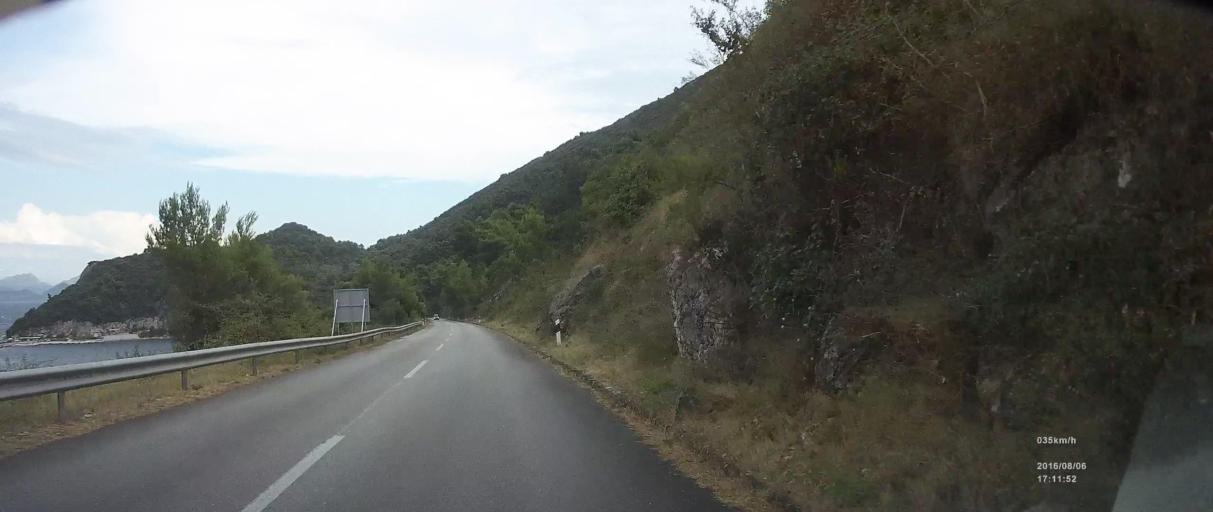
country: HR
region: Dubrovacko-Neretvanska
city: Ston
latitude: 42.7370
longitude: 17.6141
